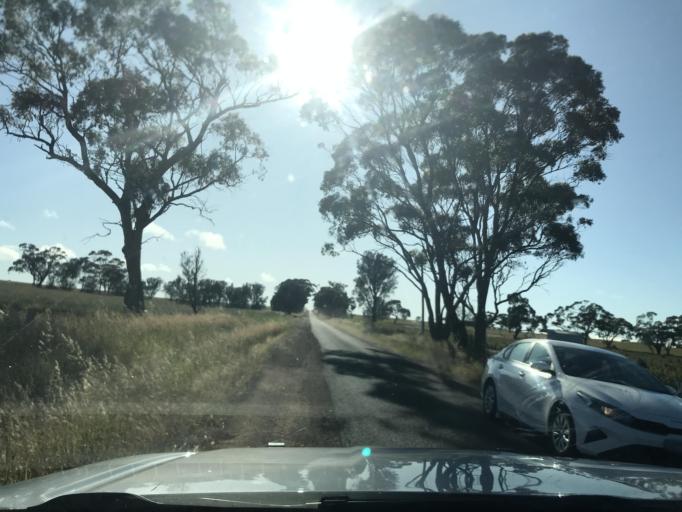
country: AU
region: Victoria
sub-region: Horsham
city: Horsham
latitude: -36.6949
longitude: 141.5726
